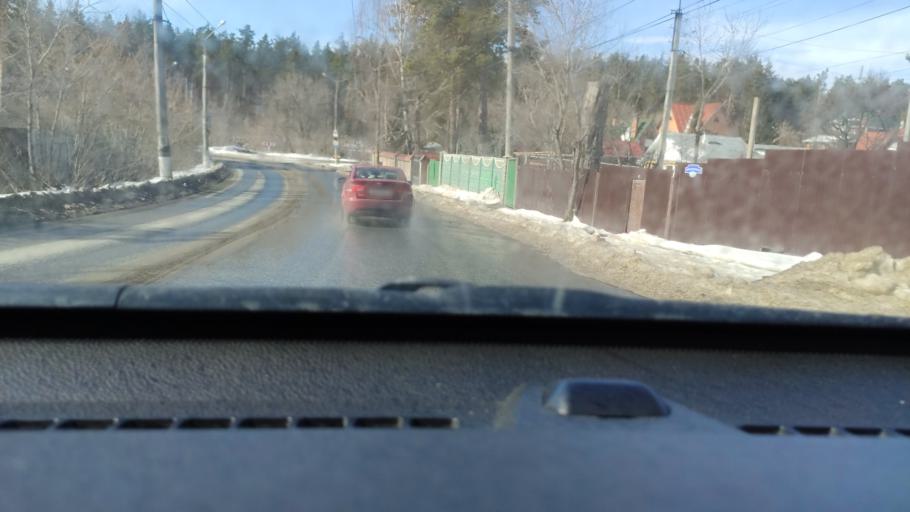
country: RU
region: Samara
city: Tol'yatti
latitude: 53.4797
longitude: 49.3501
